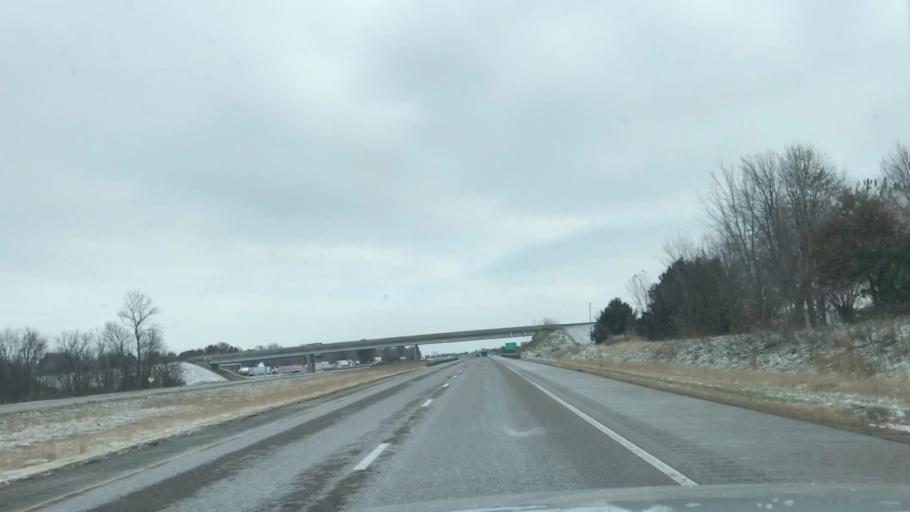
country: US
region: Illinois
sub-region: Macoupin County
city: Staunton
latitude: 38.9569
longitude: -89.7672
